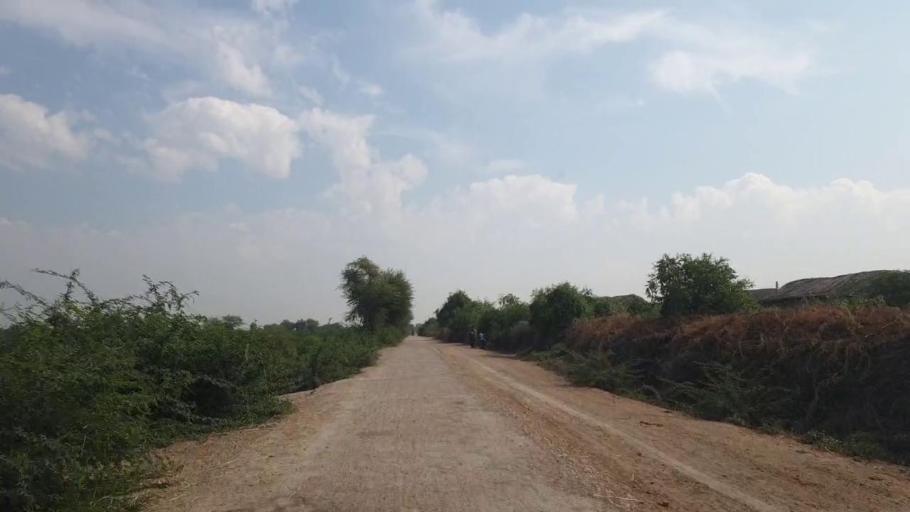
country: PK
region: Sindh
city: Rajo Khanani
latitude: 24.9369
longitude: 68.9974
